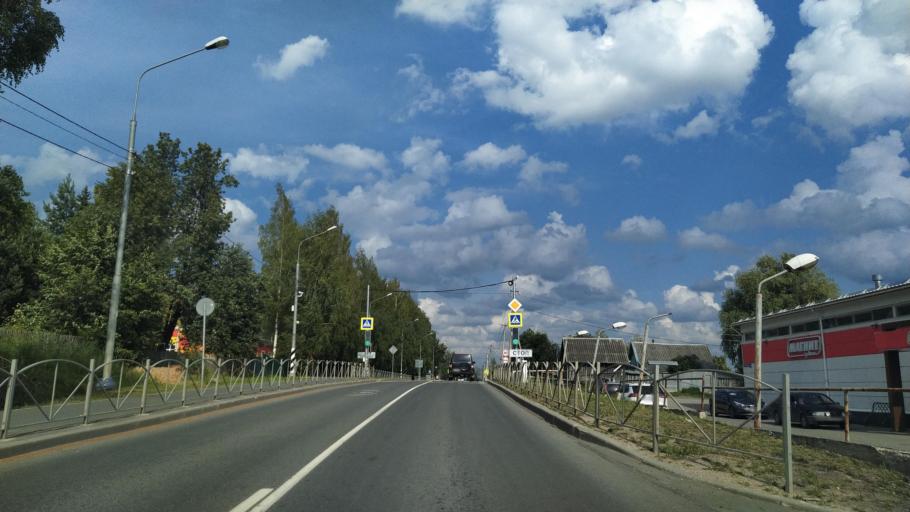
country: RU
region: Novgorod
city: Sol'tsy
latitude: 58.1253
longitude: 30.3421
